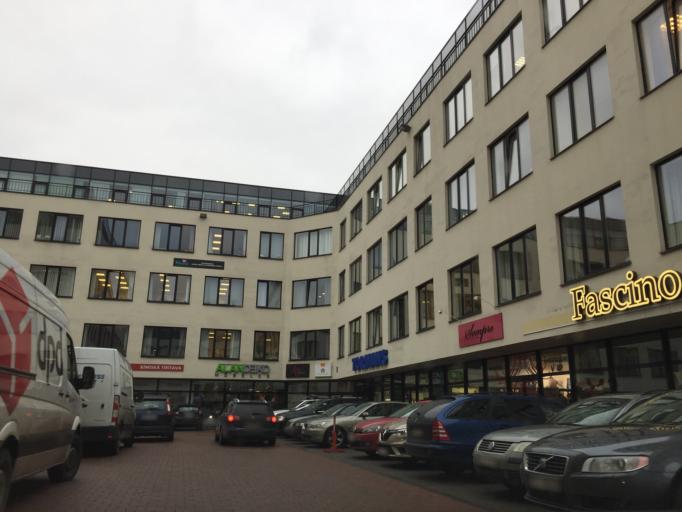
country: LV
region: Riga
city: Riga
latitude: 56.9673
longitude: 24.1417
